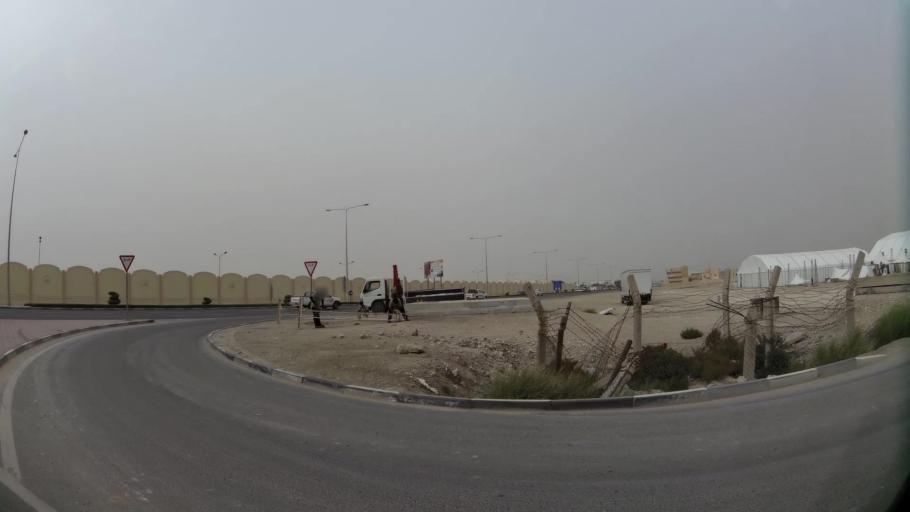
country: QA
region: Baladiyat ad Dawhah
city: Doha
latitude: 25.2537
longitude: 51.4912
